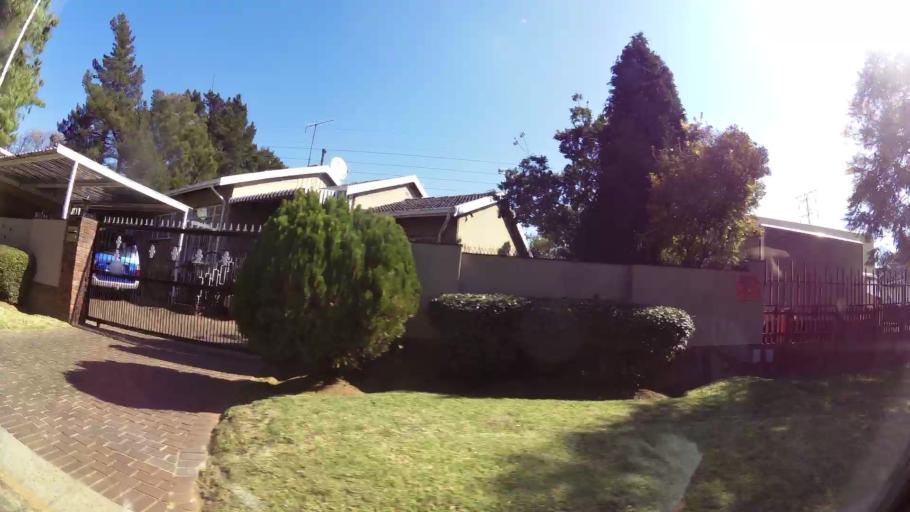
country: ZA
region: Gauteng
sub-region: City of Johannesburg Metropolitan Municipality
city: Johannesburg
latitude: -26.2735
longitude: 27.9845
